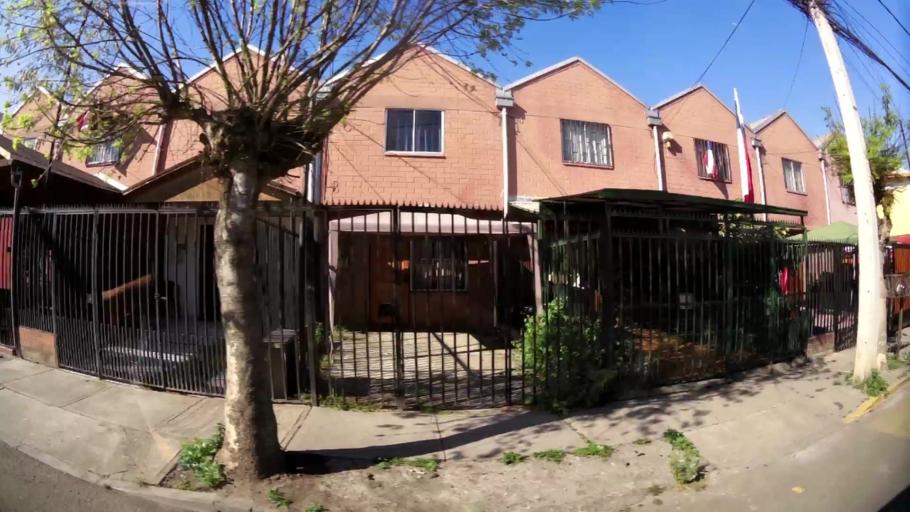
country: CL
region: Santiago Metropolitan
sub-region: Provincia de Santiago
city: Lo Prado
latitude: -33.4857
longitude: -70.7651
